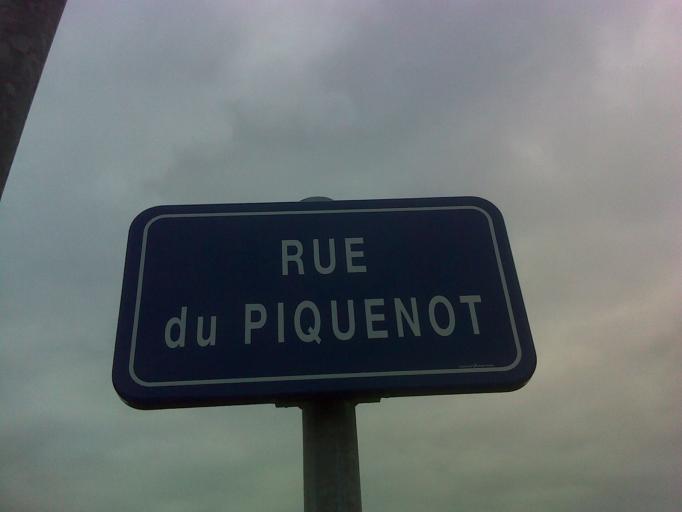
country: FR
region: Lower Normandy
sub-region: Departement de la Manche
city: Le Val-Saint-Pere
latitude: 48.6319
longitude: -1.3540
